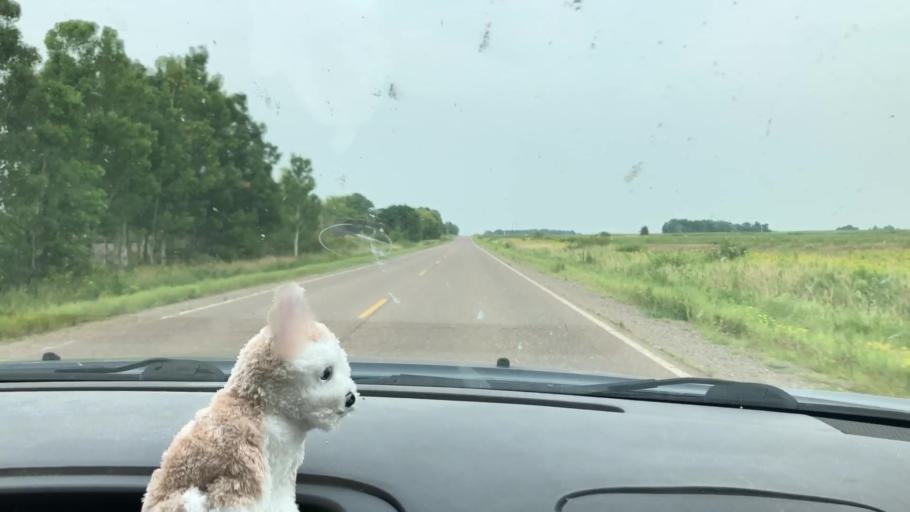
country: US
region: Wisconsin
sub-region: Chippewa County
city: Stanley
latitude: 44.9584
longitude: -90.9190
